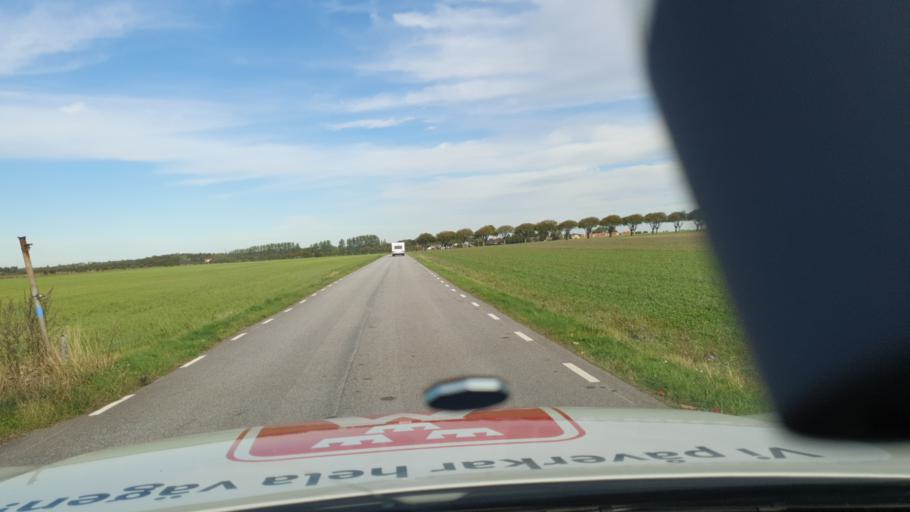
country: SE
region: Skane
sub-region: Malmo
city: Bunkeflostrand
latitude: 55.5115
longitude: 12.9370
